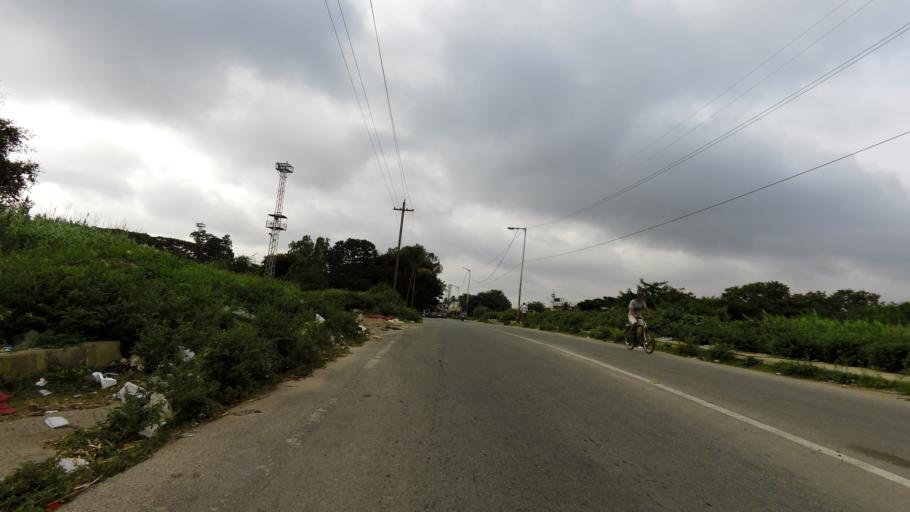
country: IN
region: Karnataka
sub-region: Bangalore Urban
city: Bangalore
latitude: 12.9975
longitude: 77.6416
